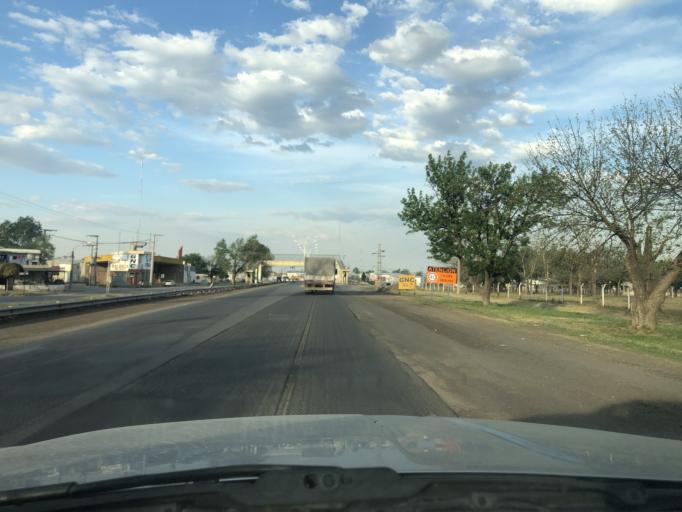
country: AR
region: Cordoba
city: Jesus Maria
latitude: -30.9882
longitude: -64.0922
